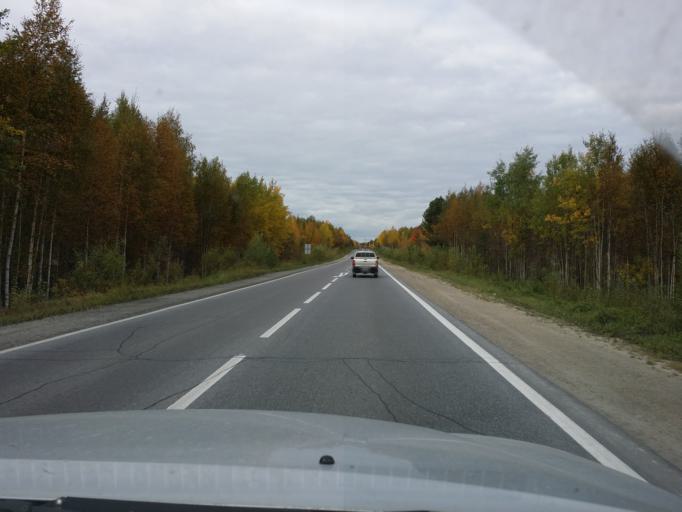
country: RU
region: Khanty-Mansiyskiy Avtonomnyy Okrug
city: Megion
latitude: 61.1604
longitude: 75.7209
